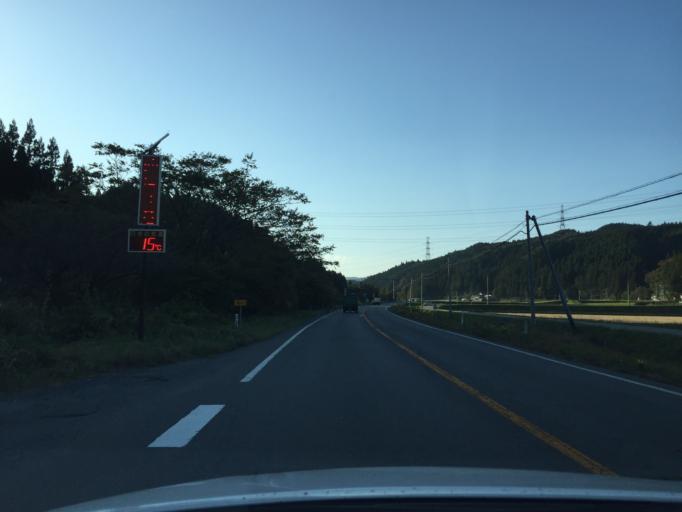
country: JP
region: Fukushima
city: Iwaki
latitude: 37.1321
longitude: 140.7148
